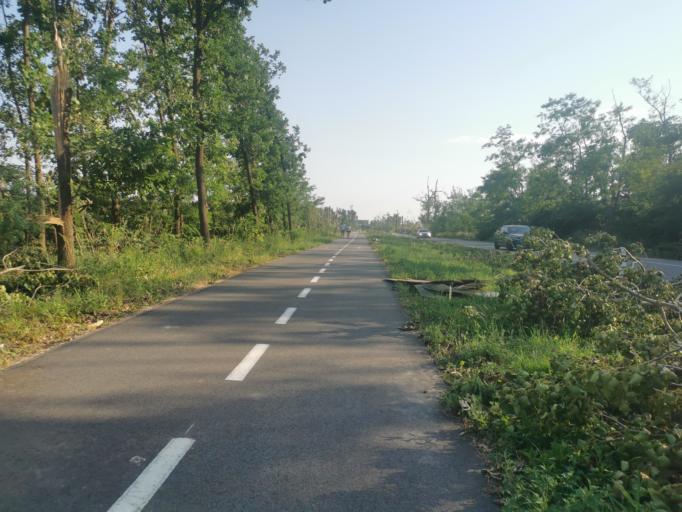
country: CZ
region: South Moravian
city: Rohatec
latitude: 48.8885
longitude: 17.1498
